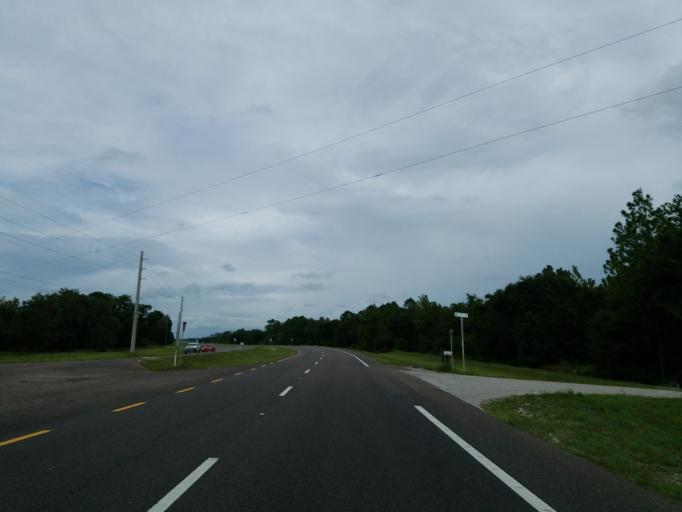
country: US
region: Florida
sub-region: Sumter County
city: Wildwood
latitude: 28.8628
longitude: -82.1567
